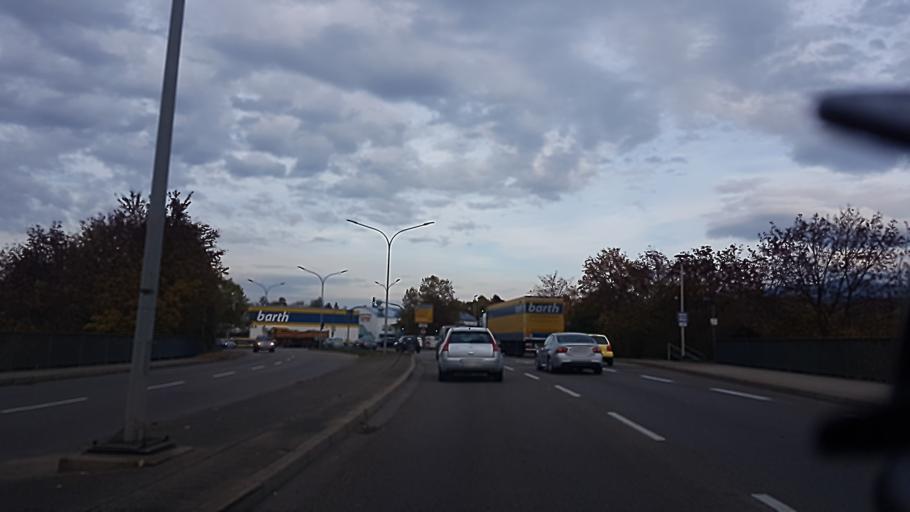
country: DE
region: Baden-Wuerttemberg
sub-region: Freiburg Region
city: Gundelfingen
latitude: 48.0352
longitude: 7.8611
